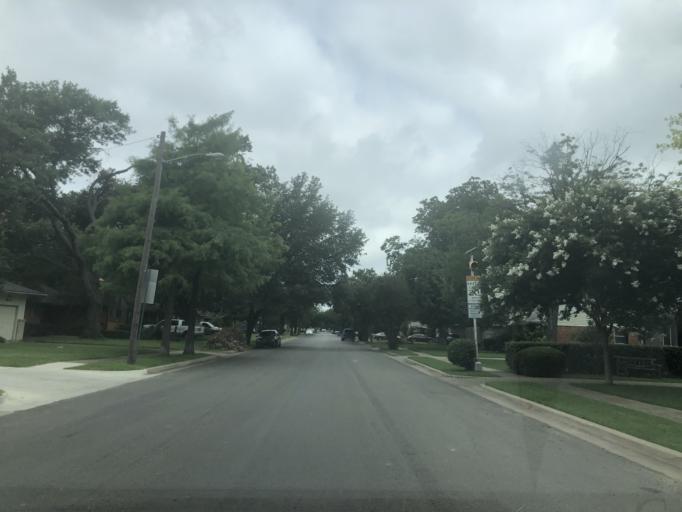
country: US
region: Texas
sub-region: Dallas County
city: University Park
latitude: 32.8706
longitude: -96.8506
